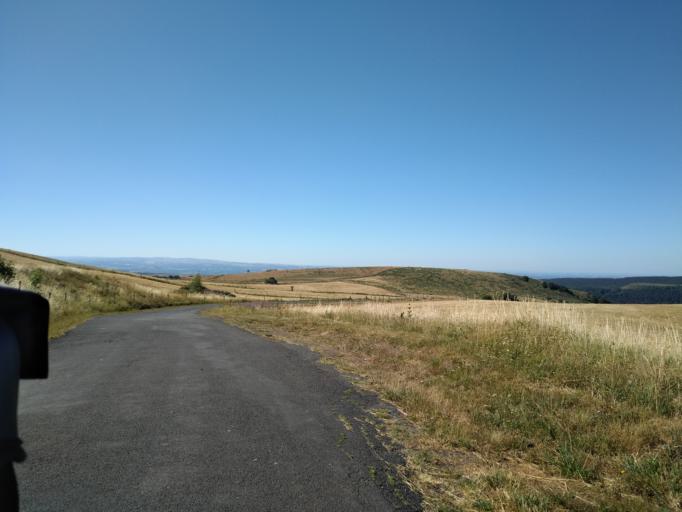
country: FR
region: Auvergne
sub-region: Departement du Cantal
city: Pierrefort
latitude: 45.0167
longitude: 2.8180
